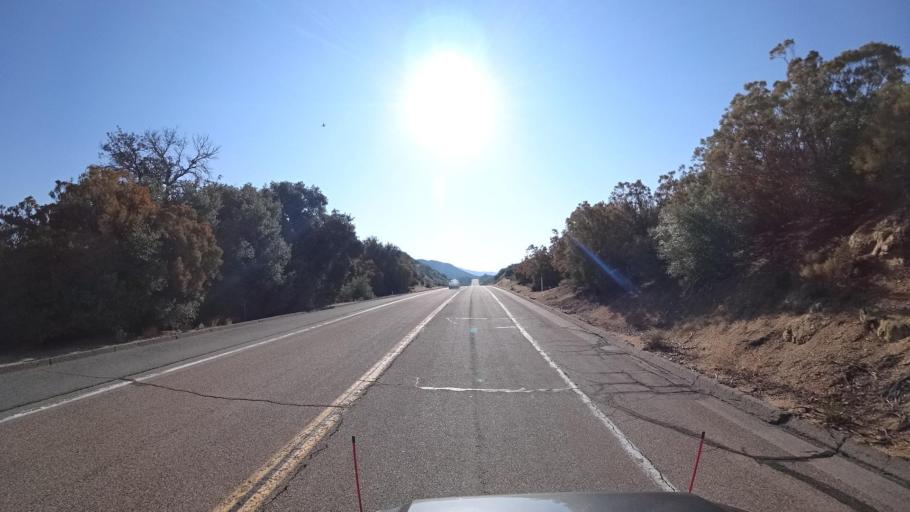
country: US
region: California
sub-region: San Diego County
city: Pine Valley
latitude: 32.8176
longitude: -116.5197
